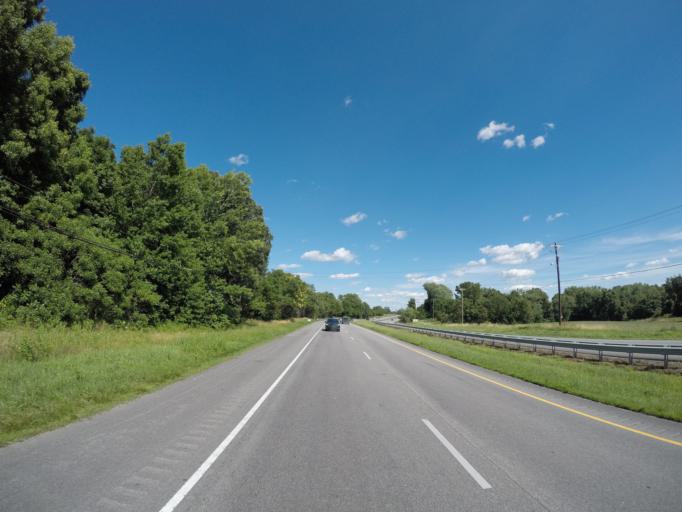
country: US
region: Maryland
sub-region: Queen Anne's County
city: Grasonville
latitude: 38.9763
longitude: -76.1297
